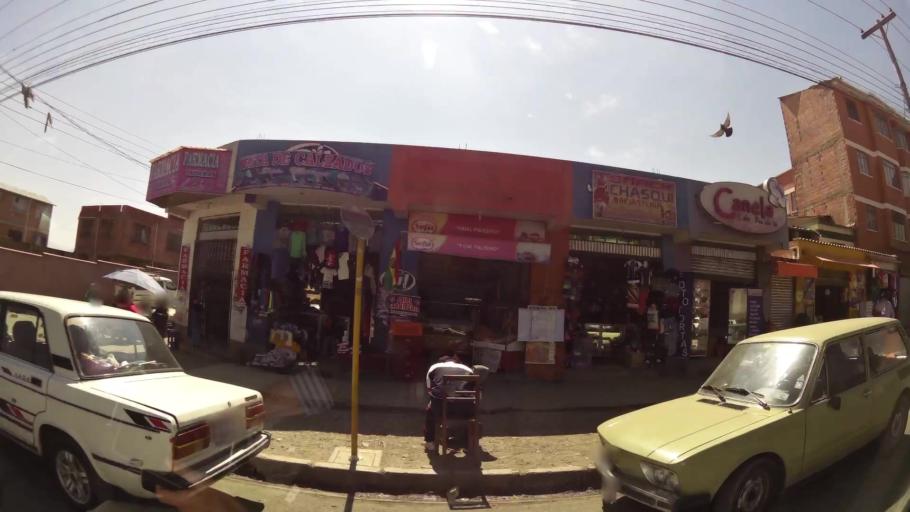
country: BO
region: La Paz
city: La Paz
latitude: -16.5371
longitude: -68.0478
